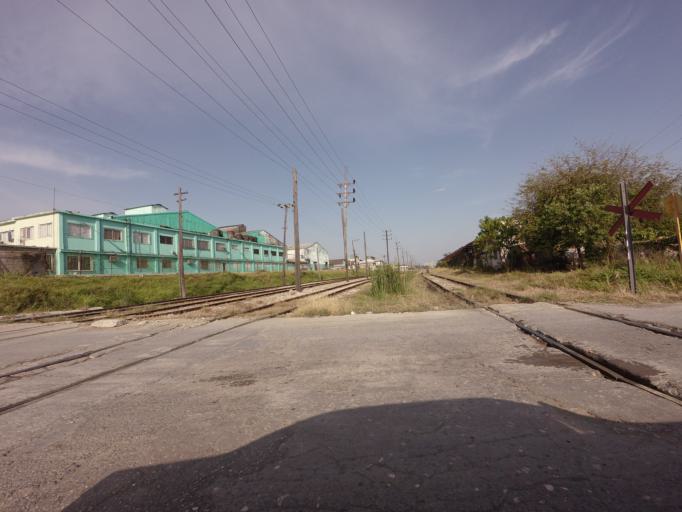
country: CU
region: La Habana
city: Regla
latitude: 23.1088
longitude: -82.3406
